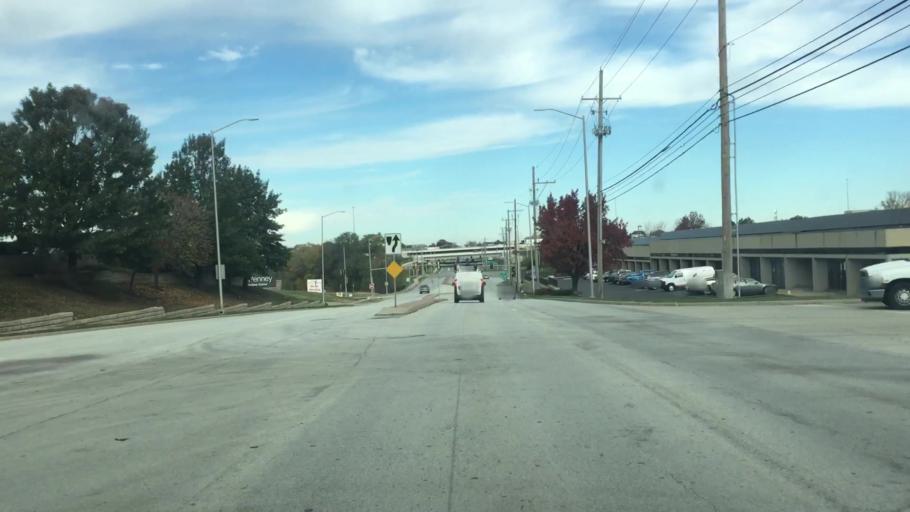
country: US
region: Kansas
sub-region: Johnson County
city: Lenexa
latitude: 38.9366
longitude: -94.7608
